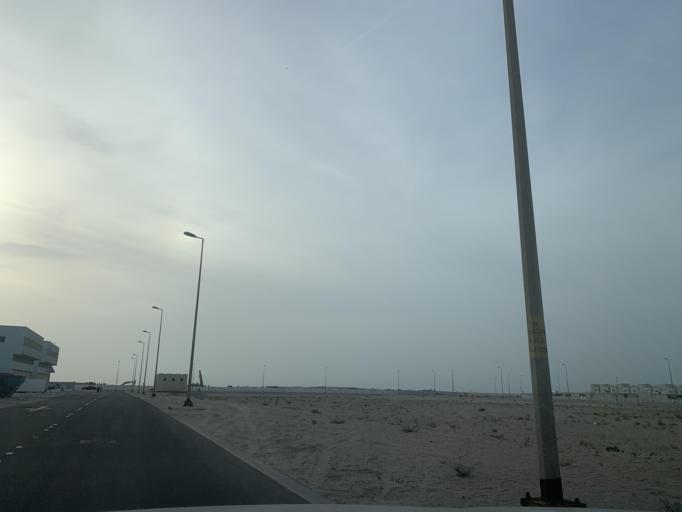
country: BH
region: Muharraq
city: Al Muharraq
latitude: 26.3095
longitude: 50.6202
